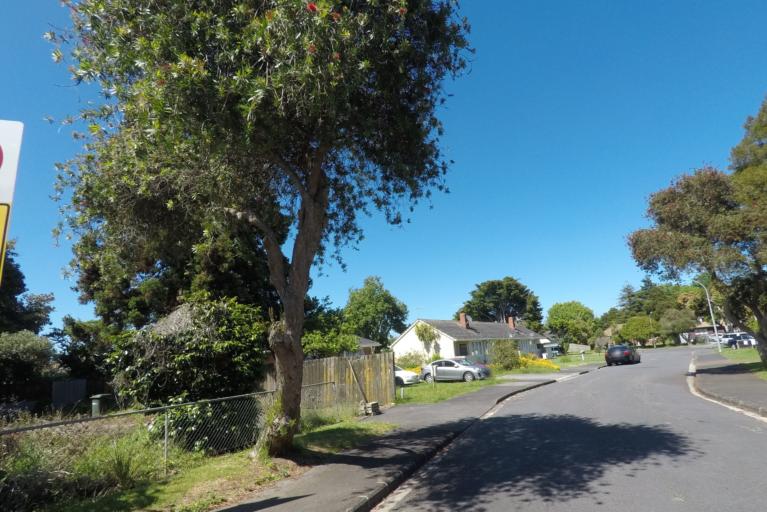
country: NZ
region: Auckland
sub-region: Auckland
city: Rosebank
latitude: -36.8904
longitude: 174.6869
